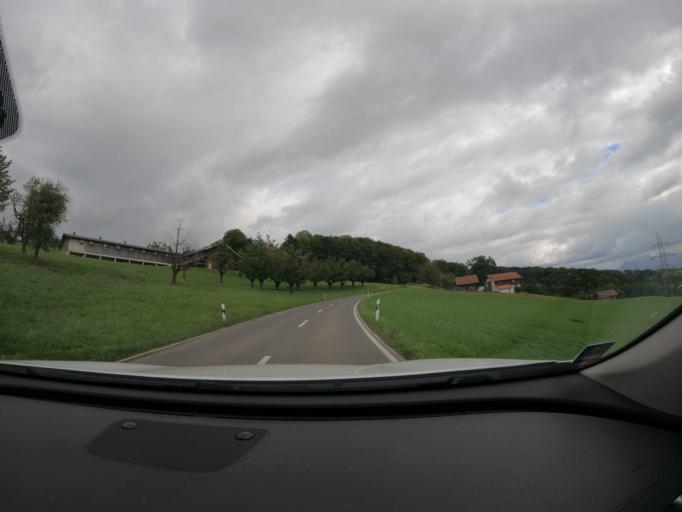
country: CH
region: Lucerne
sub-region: Sursee District
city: Bueron
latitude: 47.2224
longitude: 8.1002
